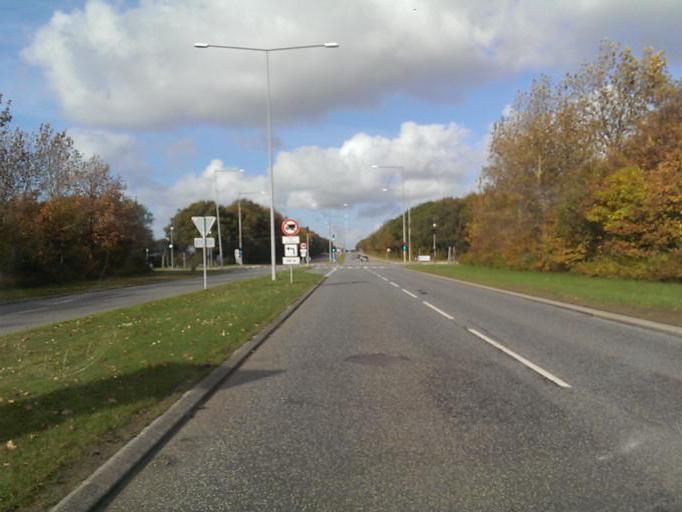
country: DK
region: South Denmark
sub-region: Esbjerg Kommune
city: Esbjerg
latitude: 55.4643
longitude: 8.4955
